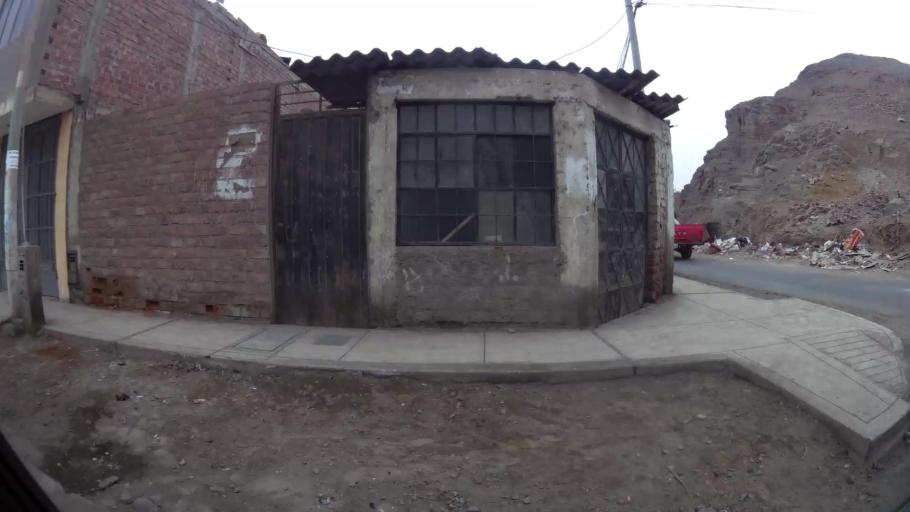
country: PE
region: Lima
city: Ventanilla
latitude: -11.9355
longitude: -77.0870
